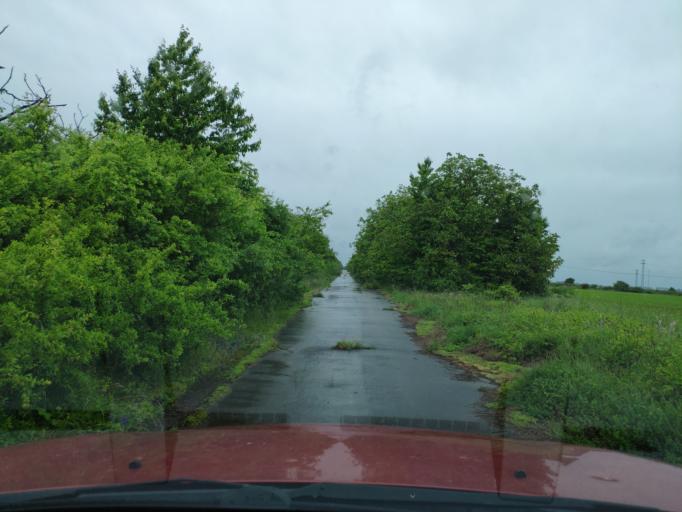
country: SK
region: Kosicky
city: Cierna nad Tisou
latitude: 48.4194
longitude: 22.0566
